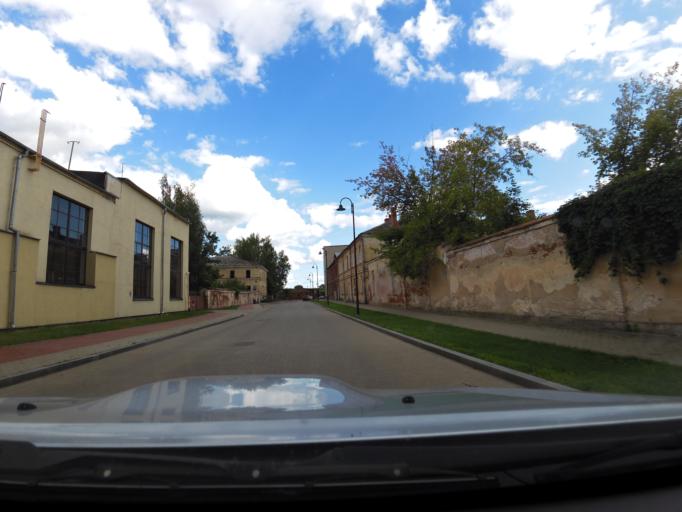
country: LV
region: Daugavpils
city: Daugavpils
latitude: 55.8873
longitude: 26.4974
